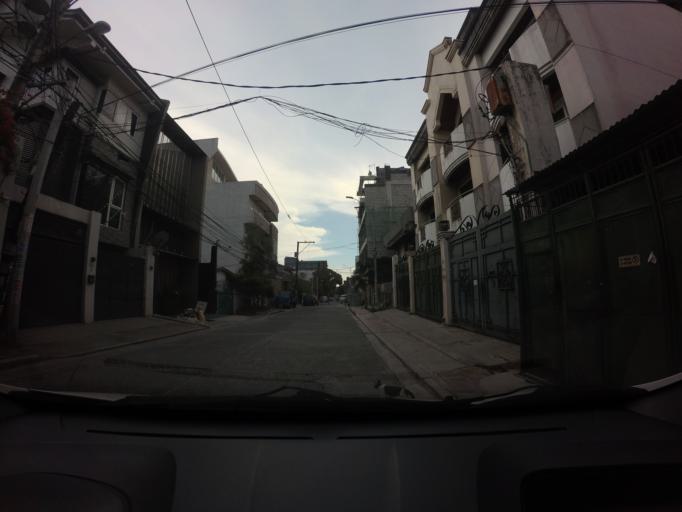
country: PH
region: Calabarzon
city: Del Monte
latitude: 14.6167
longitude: 121.0074
